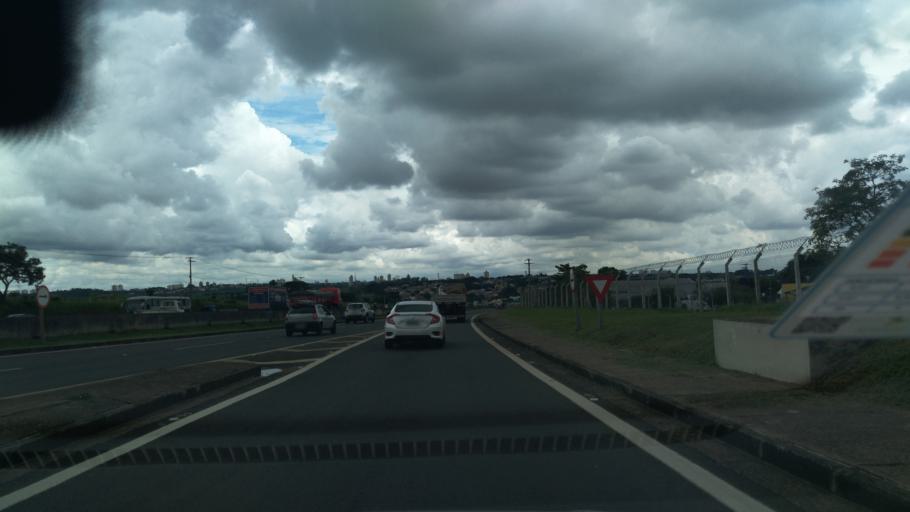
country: BR
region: Sao Paulo
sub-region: Campinas
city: Campinas
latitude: -22.8744
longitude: -47.1247
